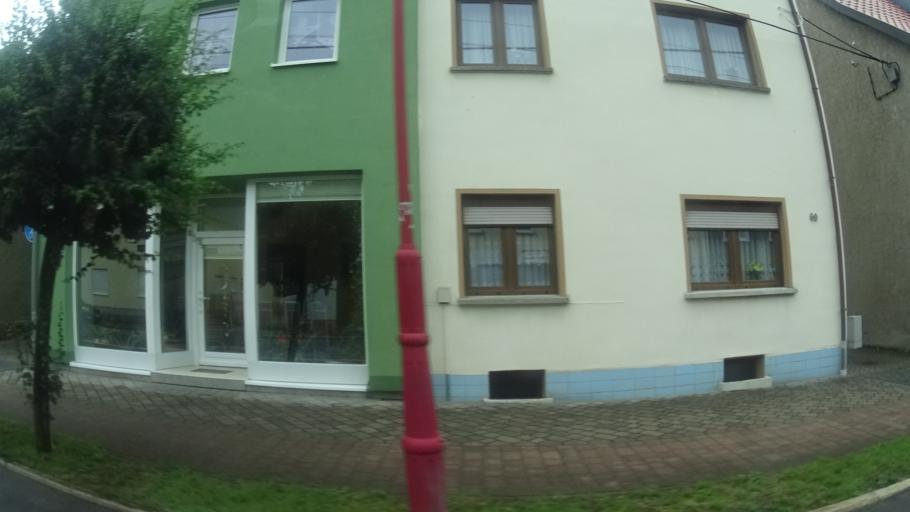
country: DE
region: Thuringia
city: Langewiesen
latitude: 50.6720
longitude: 10.9751
